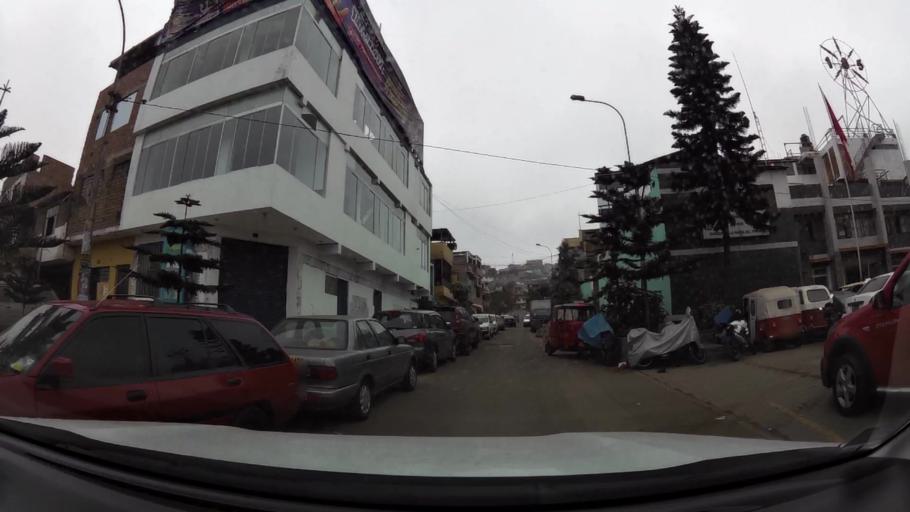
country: PE
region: Lima
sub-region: Lima
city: Surco
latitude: -12.1673
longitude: -76.9516
